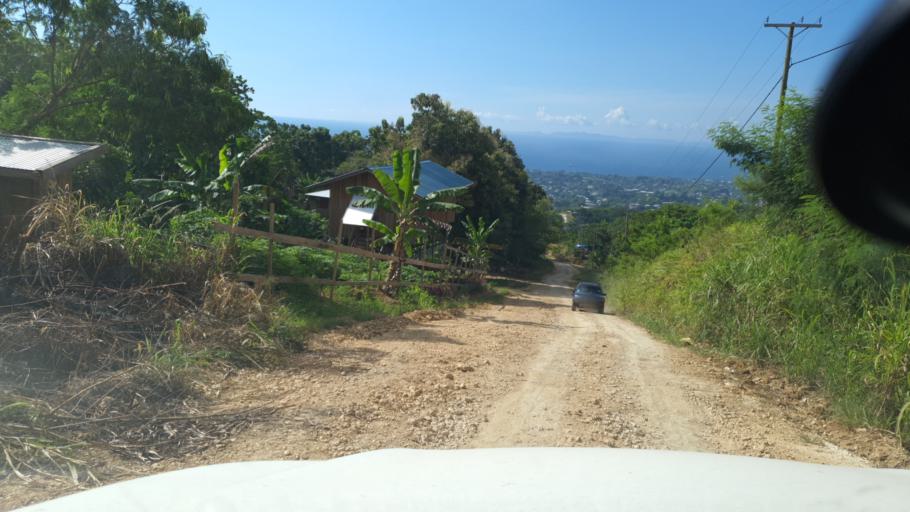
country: SB
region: Guadalcanal
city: Honiara
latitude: -9.4640
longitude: 159.9750
